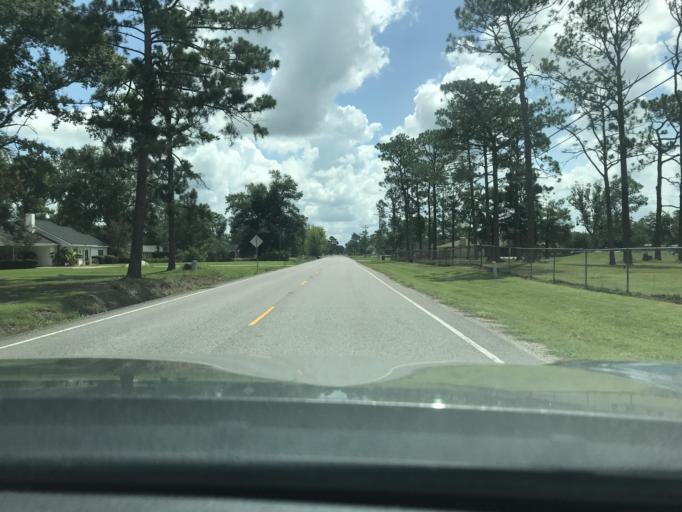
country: US
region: Louisiana
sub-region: Calcasieu Parish
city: Moss Bluff
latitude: 30.3447
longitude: -93.2232
